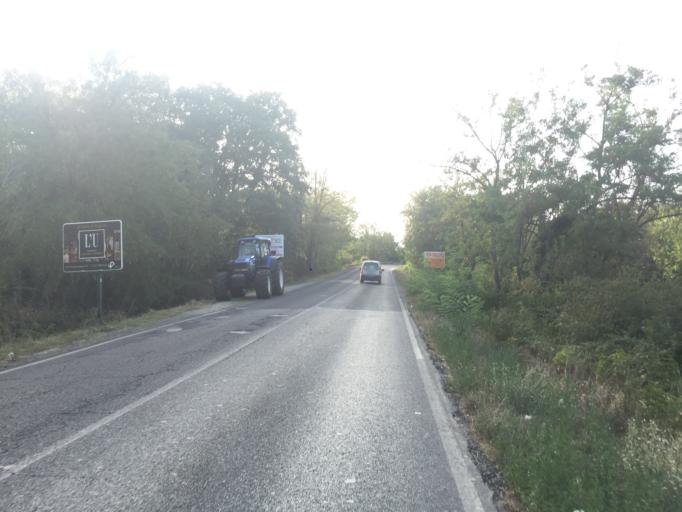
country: IT
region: Umbria
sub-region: Provincia di Perugia
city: Torgiano
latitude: 43.0336
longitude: 12.4246
